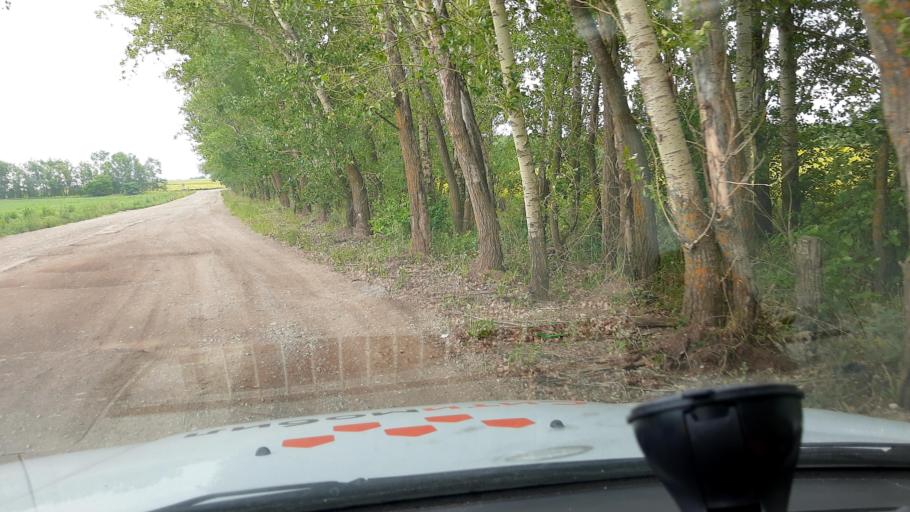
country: RU
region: Bashkortostan
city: Avdon
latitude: 54.6546
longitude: 55.6633
